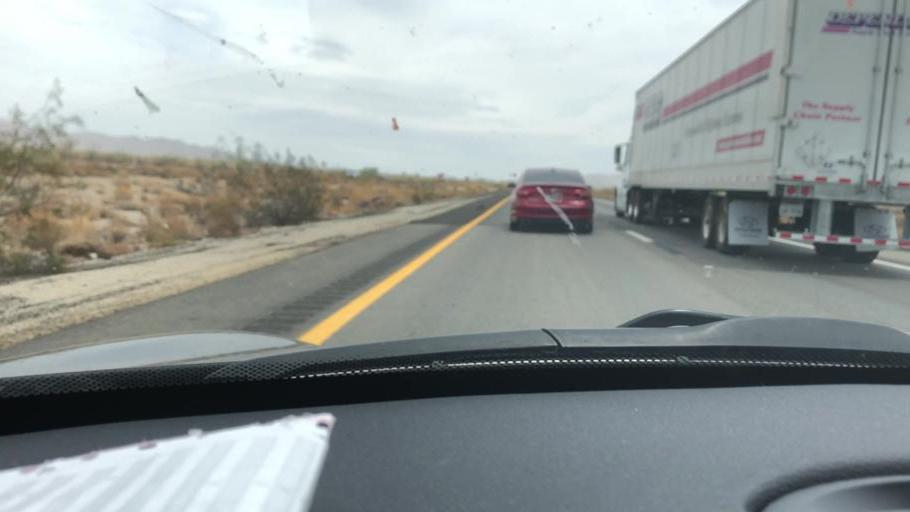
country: US
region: California
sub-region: Riverside County
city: Mecca
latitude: 33.6621
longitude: -115.8414
